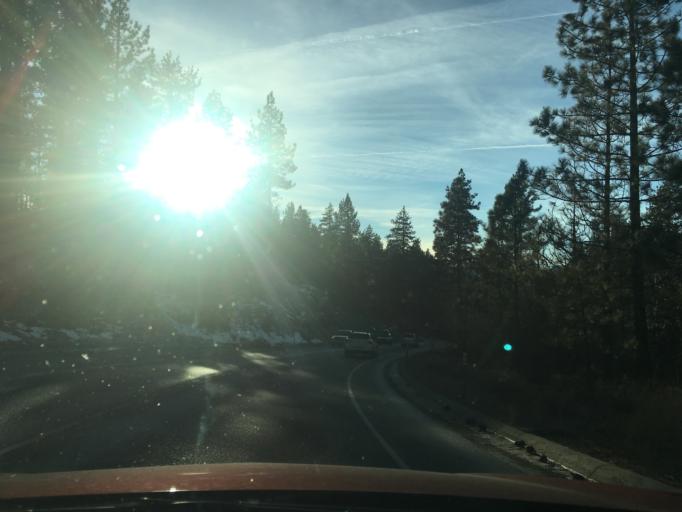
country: US
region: Nevada
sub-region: Douglas County
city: Kingsbury
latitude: 38.9676
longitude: -119.9179
